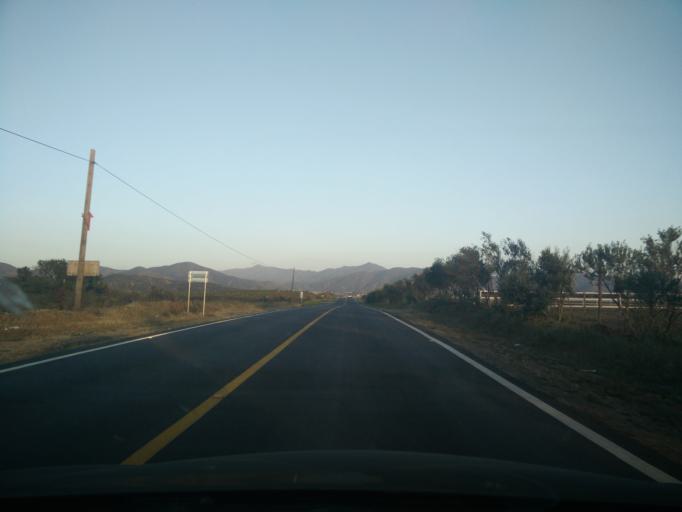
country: MX
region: Baja California
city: El Sauzal
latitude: 32.0026
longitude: -116.6693
